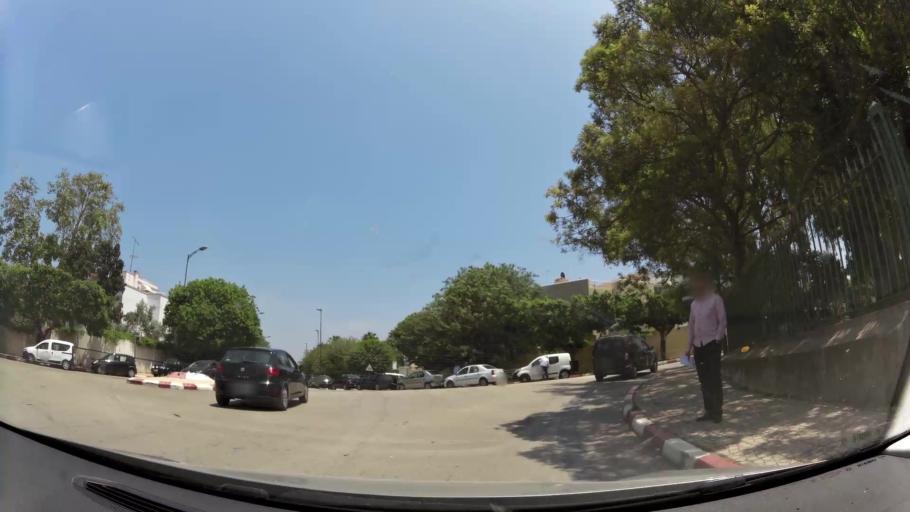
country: MA
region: Rabat-Sale-Zemmour-Zaer
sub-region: Rabat
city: Rabat
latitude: 34.0137
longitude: -6.8258
